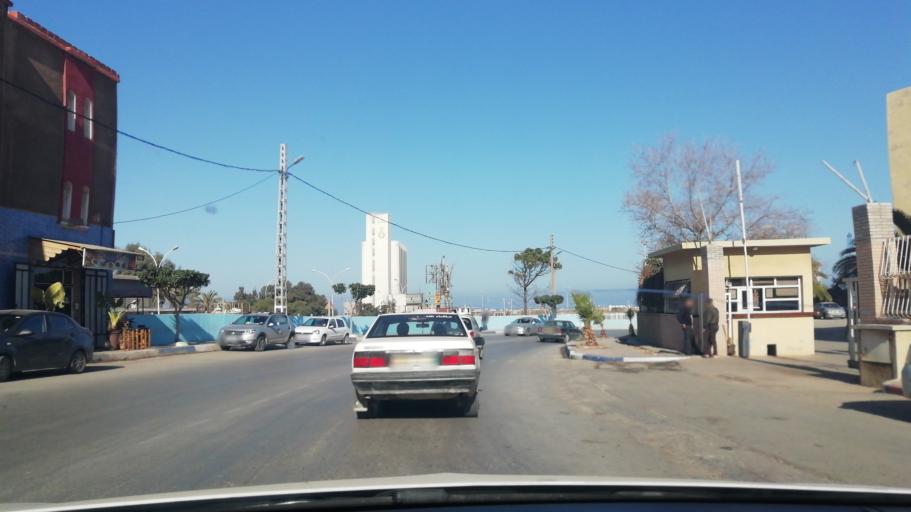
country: DZ
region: Tlemcen
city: Nedroma
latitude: 35.0979
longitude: -1.8636
